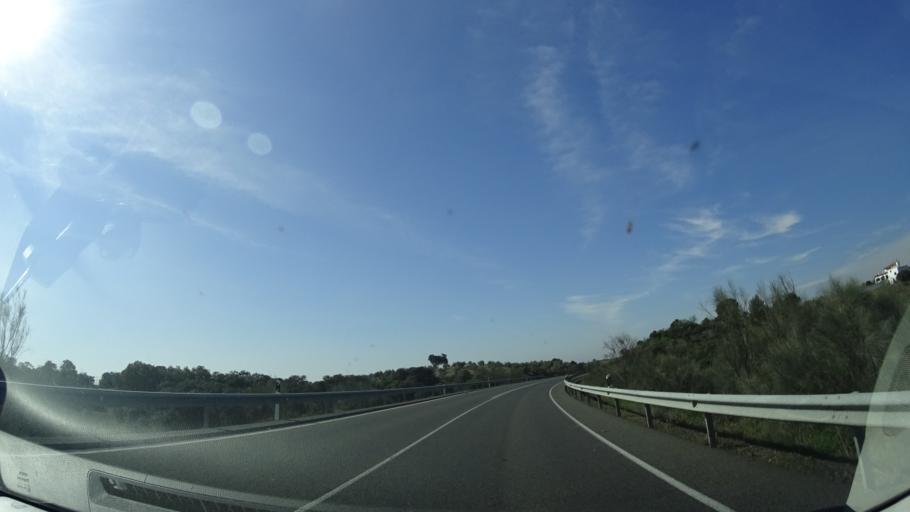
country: ES
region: Andalusia
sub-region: Province of Cordoba
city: Montoro
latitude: 38.0997
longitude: -4.3590
